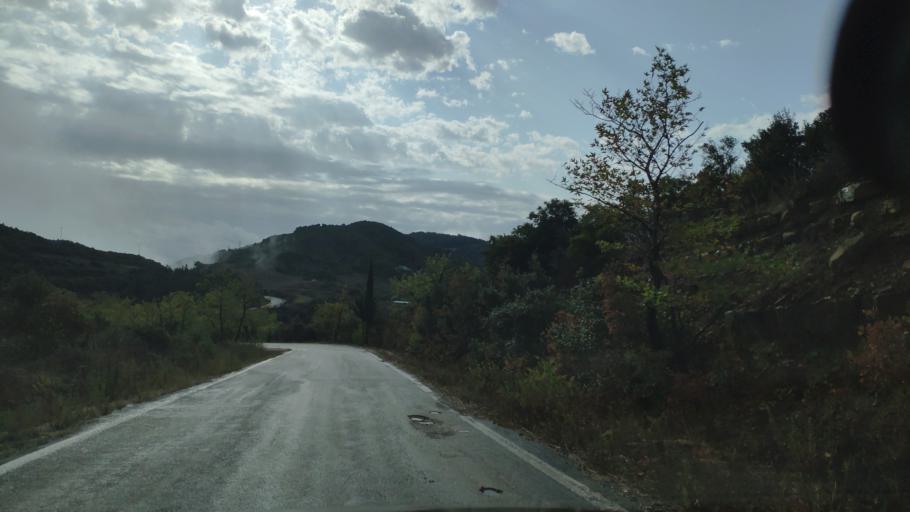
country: GR
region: West Greece
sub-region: Nomos Aitolias kai Akarnanias
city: Sardinia
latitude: 38.8737
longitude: 21.2749
